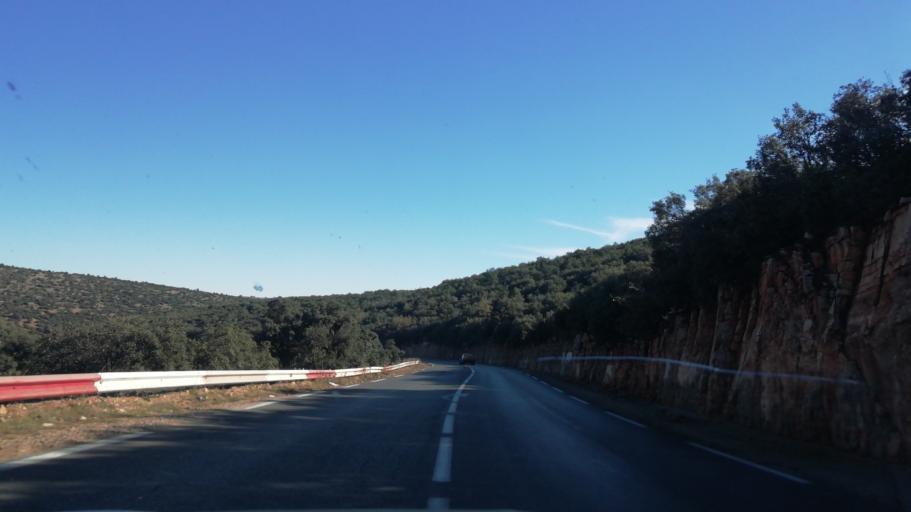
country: DZ
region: Tlemcen
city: Sebdou
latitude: 34.7411
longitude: -1.3464
